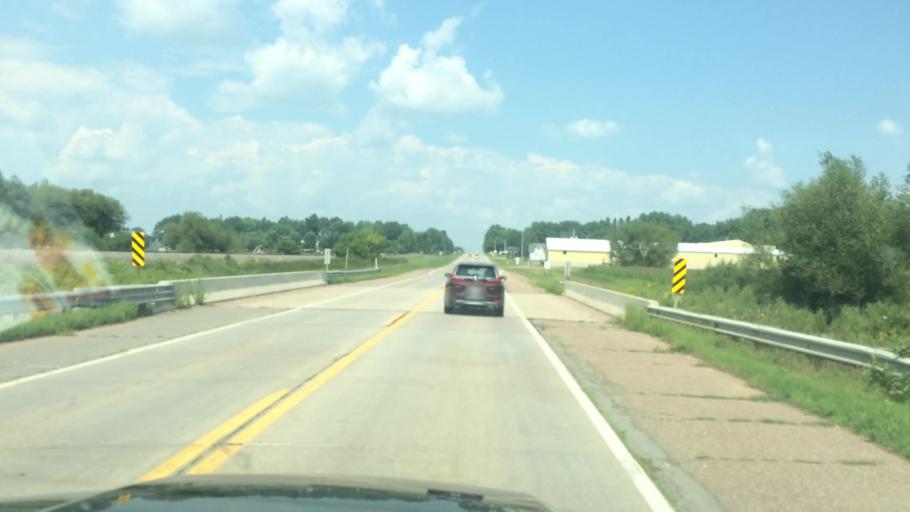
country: US
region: Wisconsin
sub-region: Clark County
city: Colby
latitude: 44.8424
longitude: -90.3159
